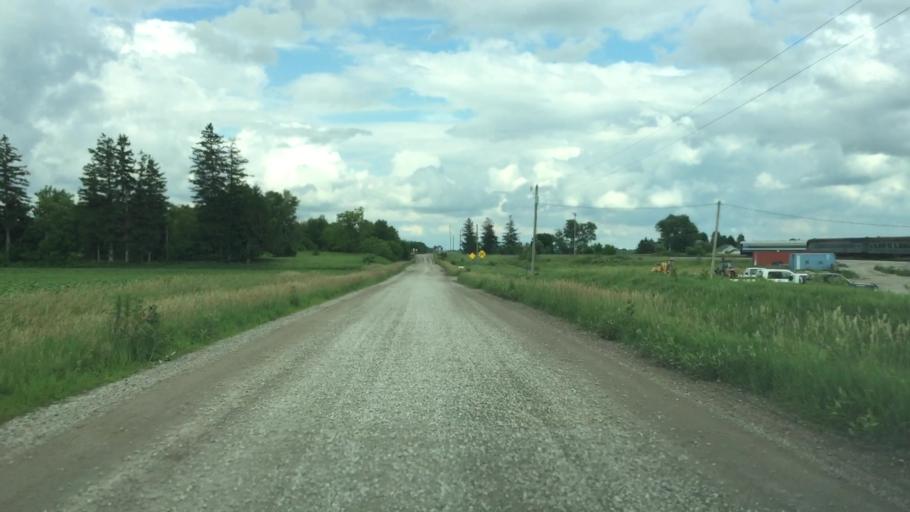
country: US
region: Iowa
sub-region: Jasper County
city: Newton
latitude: 41.7353
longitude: -93.0135
